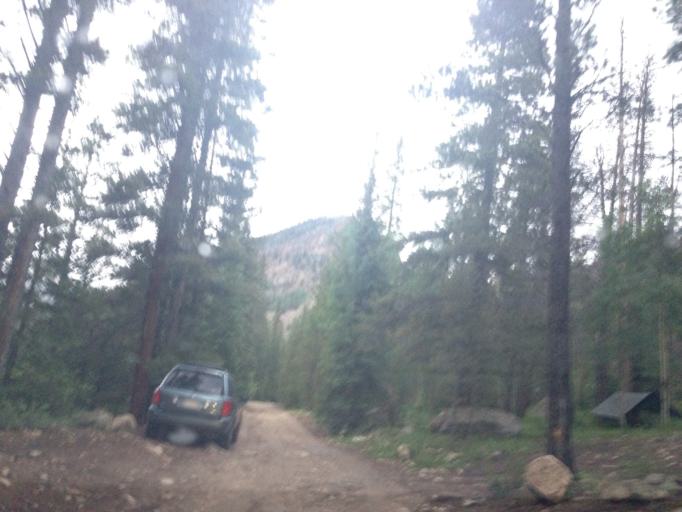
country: US
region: Colorado
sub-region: Clear Creek County
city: Georgetown
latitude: 39.5619
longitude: -105.7648
